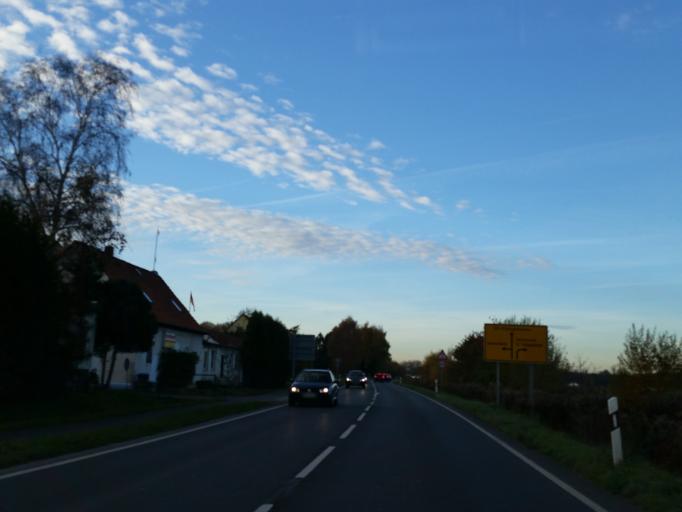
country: DE
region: Lower Saxony
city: Cremlingen
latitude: 52.2485
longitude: 10.5987
